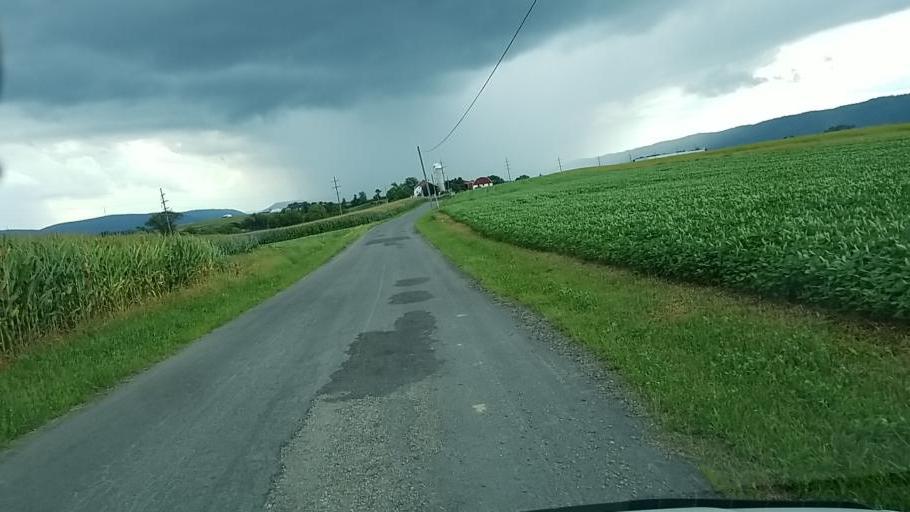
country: US
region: Pennsylvania
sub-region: Dauphin County
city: Elizabethville
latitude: 40.5814
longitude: -76.8505
